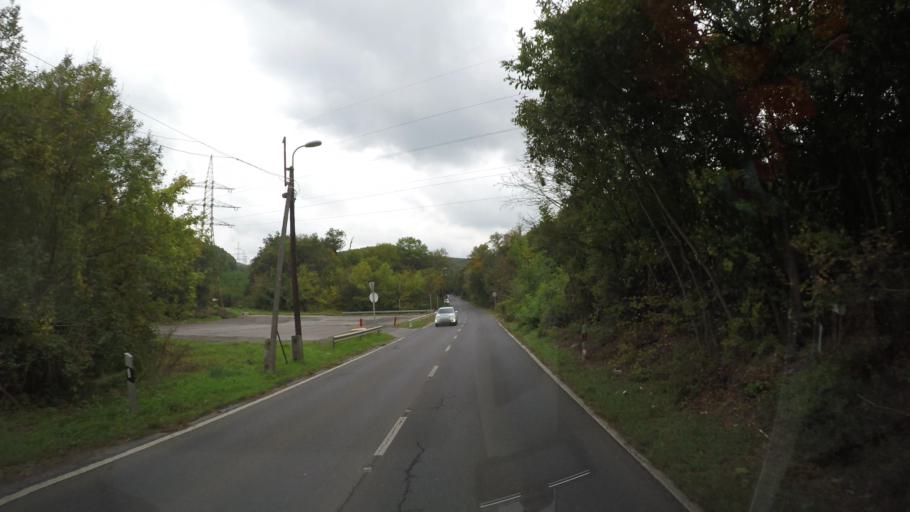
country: HU
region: Pest
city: Budakeszi
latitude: 47.5398
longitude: 18.9574
